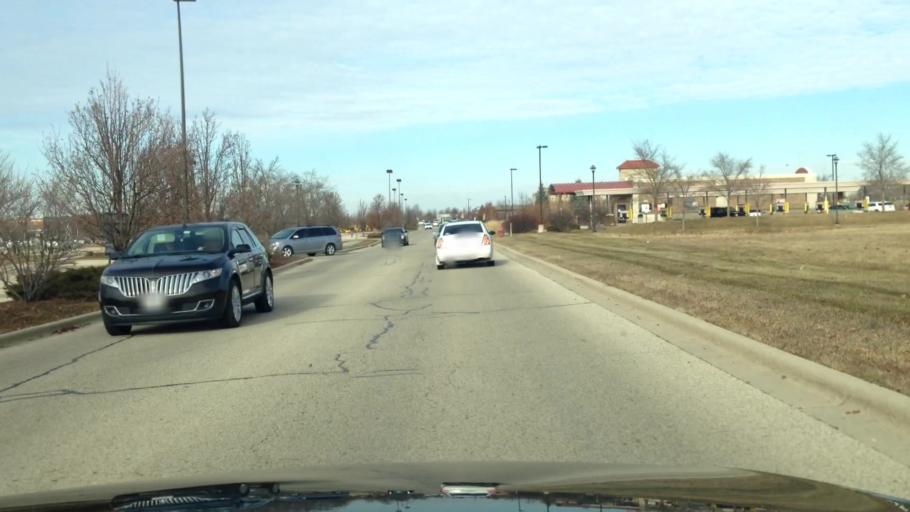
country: US
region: Illinois
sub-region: McHenry County
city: Lake in the Hills
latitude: 42.1582
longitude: -88.3369
